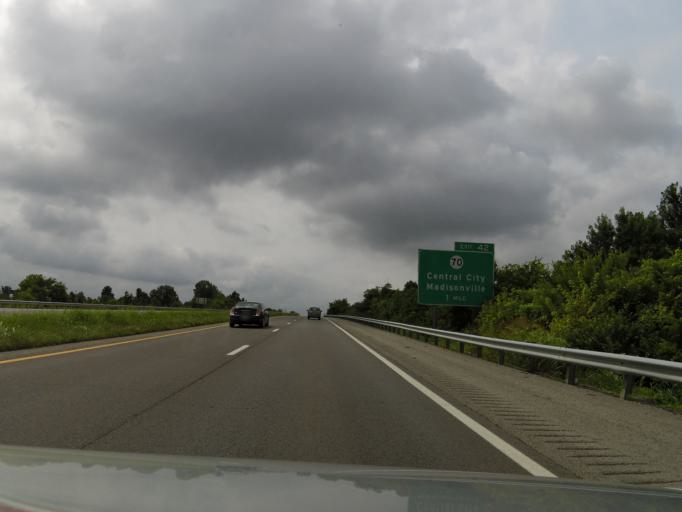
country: US
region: Kentucky
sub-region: Hopkins County
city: Madisonville
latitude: 37.3430
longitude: -87.4812
